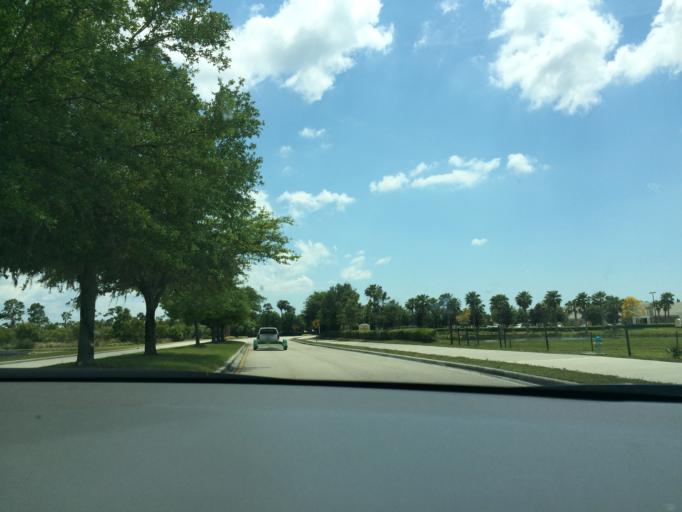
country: US
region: Florida
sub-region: Sarasota County
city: The Meadows
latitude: 27.3853
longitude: -82.4244
